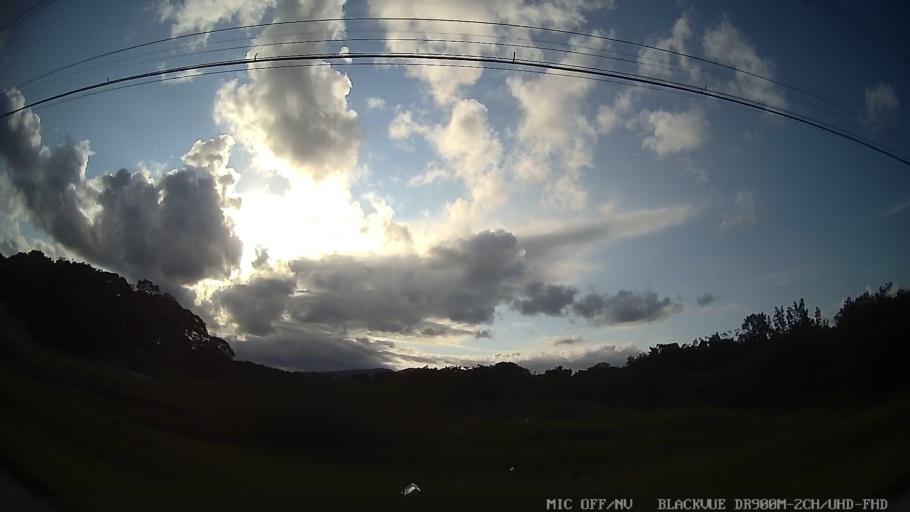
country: BR
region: Sao Paulo
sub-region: Itanhaem
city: Itanhaem
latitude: -24.1550
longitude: -46.8253
